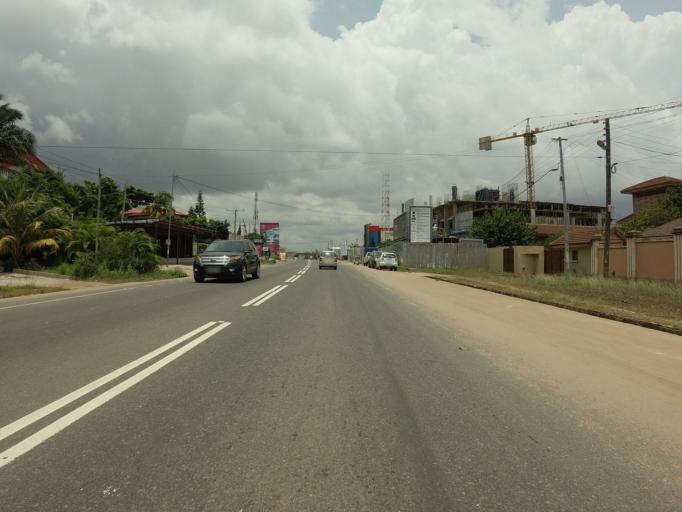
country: GH
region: Greater Accra
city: Medina Estates
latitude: 5.6377
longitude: -0.1435
